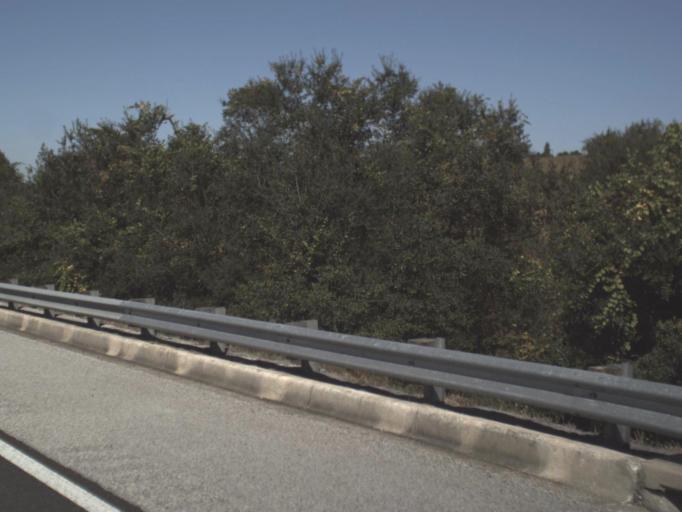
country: US
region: Florida
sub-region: Lake County
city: Minneola
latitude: 28.6164
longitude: -81.7400
